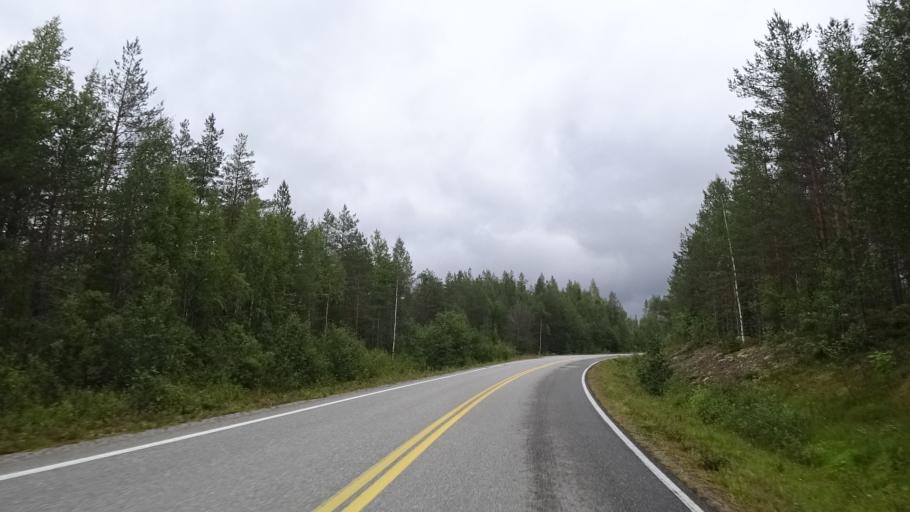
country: FI
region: North Karelia
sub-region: Joensuu
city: Ilomantsi
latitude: 63.2537
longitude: 30.7381
